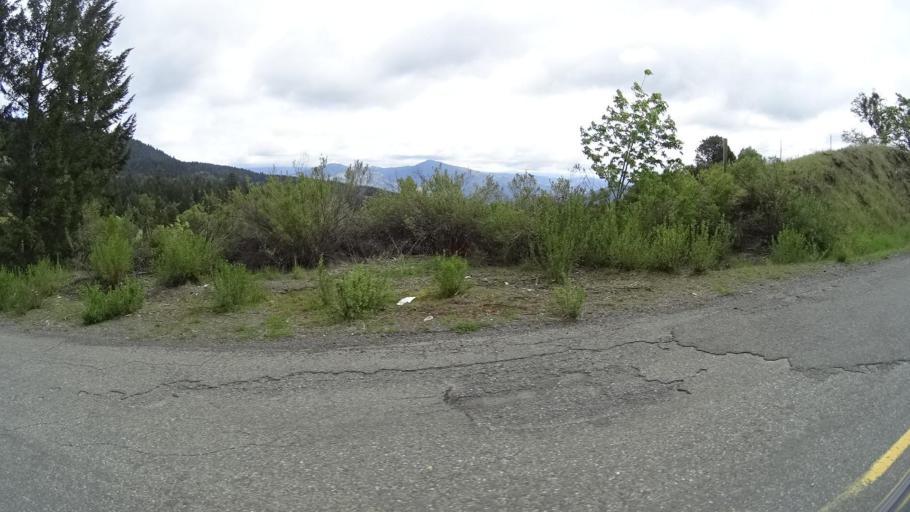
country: US
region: California
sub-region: Humboldt County
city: Redway
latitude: 40.1137
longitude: -123.6725
